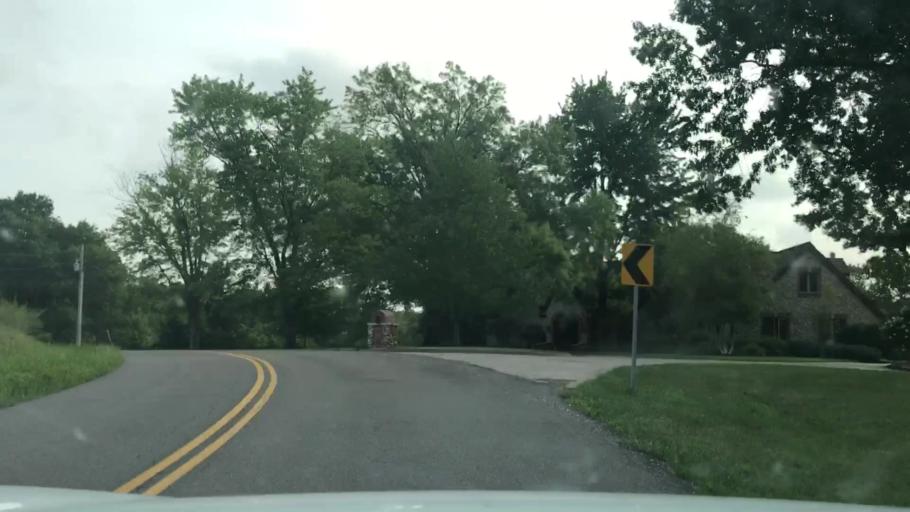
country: US
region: Missouri
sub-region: Saint Charles County
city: Cottleville
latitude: 38.7056
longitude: -90.6419
